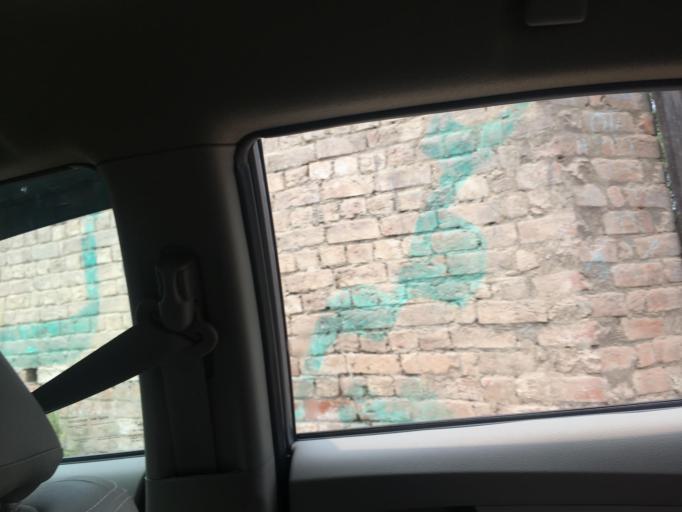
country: PK
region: Punjab
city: Lahore
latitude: 31.6187
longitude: 74.3540
